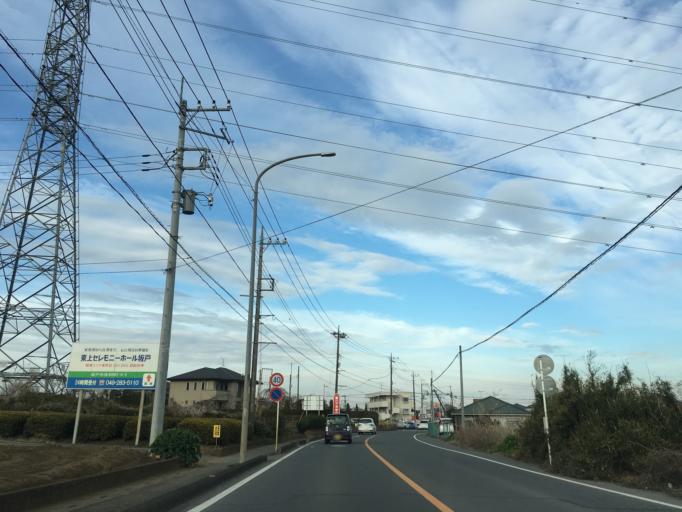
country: JP
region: Saitama
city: Sakado
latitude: 35.8982
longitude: 139.3679
